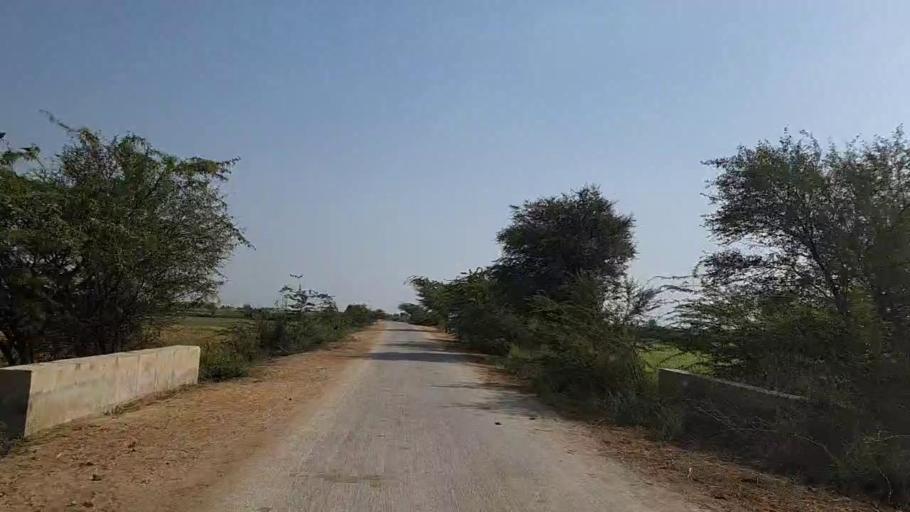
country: PK
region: Sindh
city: Daro Mehar
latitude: 24.7694
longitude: 68.1816
